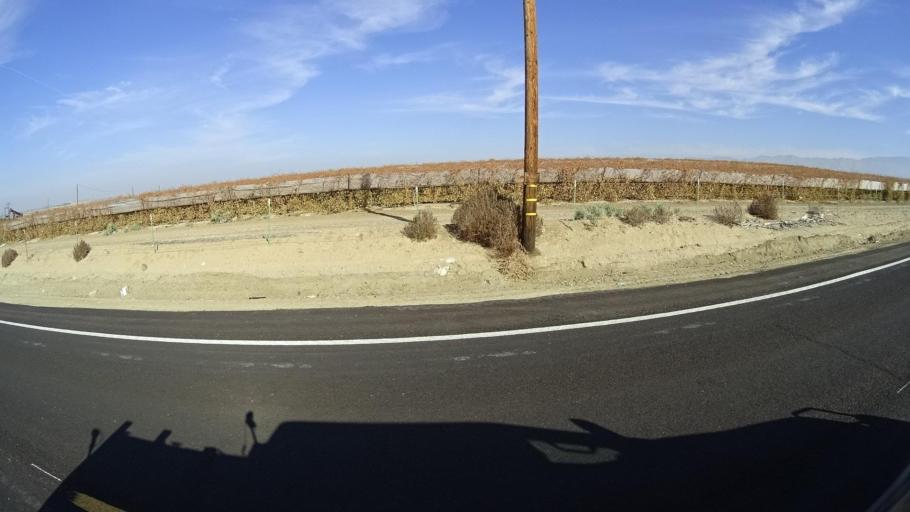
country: US
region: California
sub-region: Kern County
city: Lamont
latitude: 35.3619
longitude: -118.8690
